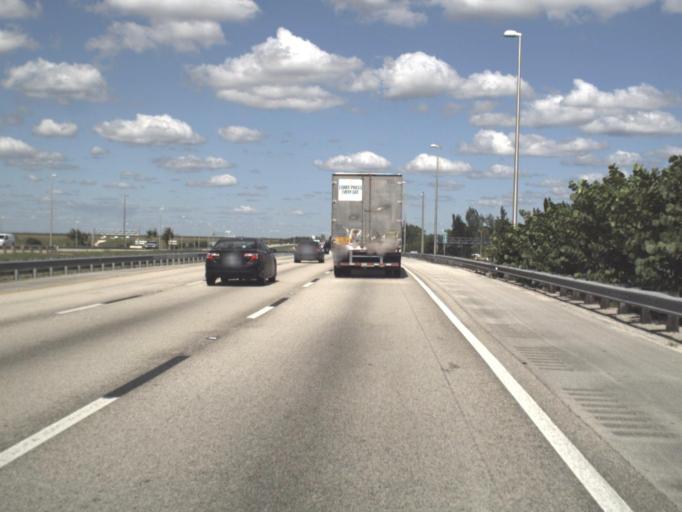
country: US
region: Florida
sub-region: Broward County
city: Coral Springs
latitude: 26.2733
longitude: -80.2964
